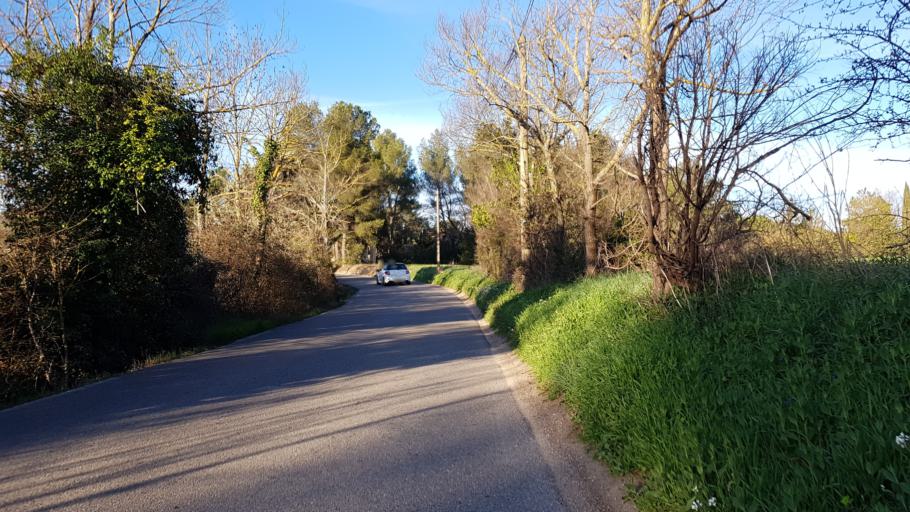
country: FR
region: Provence-Alpes-Cote d'Azur
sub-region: Departement des Bouches-du-Rhone
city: Bouc-Bel-Air
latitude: 43.4989
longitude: 5.3989
